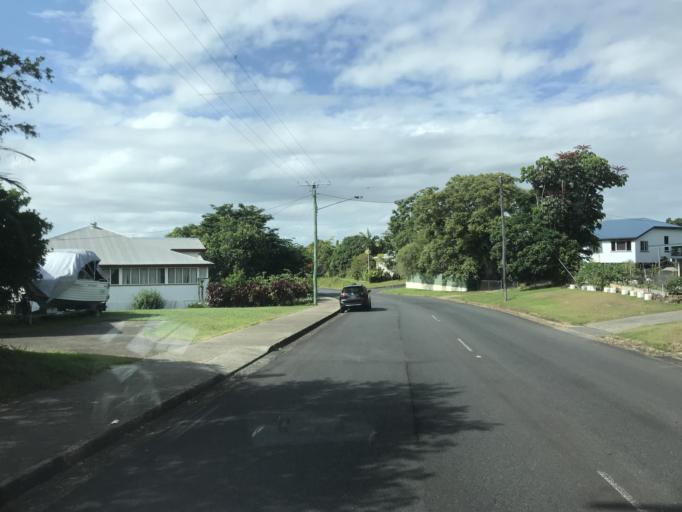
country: AU
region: Queensland
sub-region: Cassowary Coast
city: Innisfail
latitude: -17.5309
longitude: 146.0343
